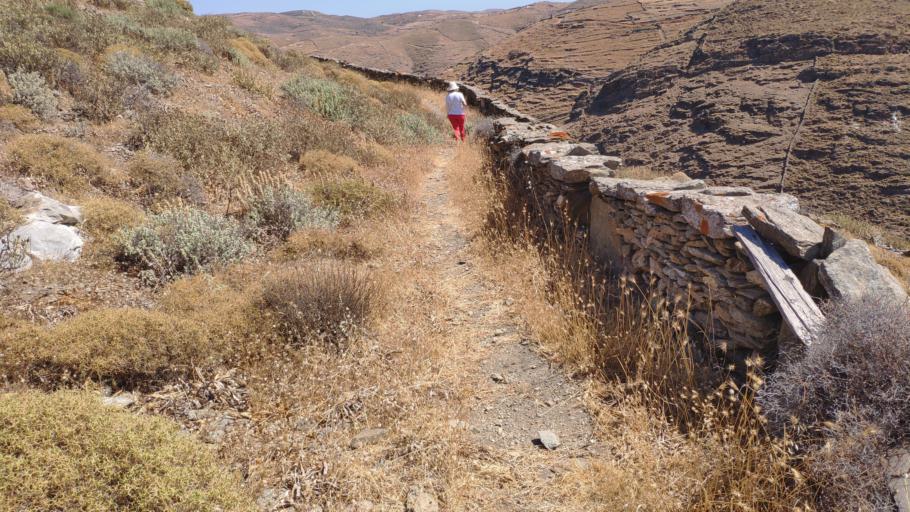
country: GR
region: South Aegean
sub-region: Nomos Kykladon
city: Kythnos
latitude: 37.4058
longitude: 24.3979
